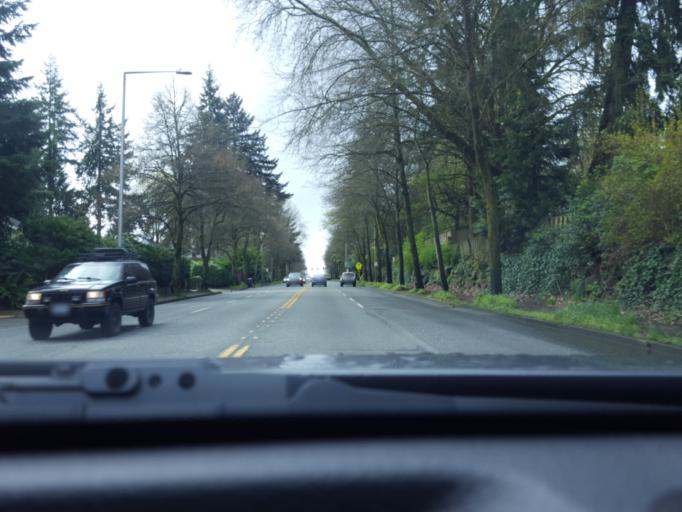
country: US
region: Washington
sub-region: King County
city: Shoreline
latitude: 47.7243
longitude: -122.3127
